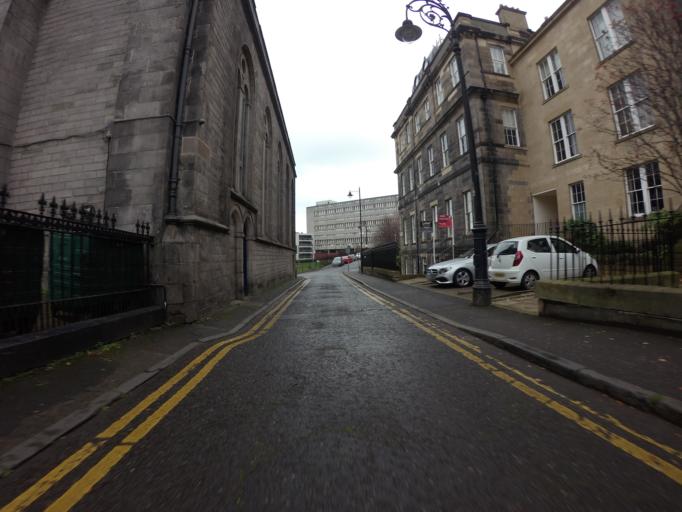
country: GB
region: Scotland
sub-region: West Lothian
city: Seafield
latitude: 55.9745
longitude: -3.1757
